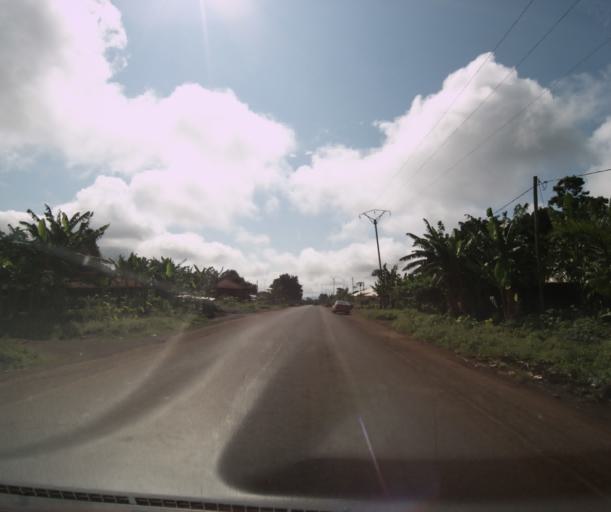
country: CM
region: West
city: Bafoussam
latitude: 5.4824
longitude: 10.4808
